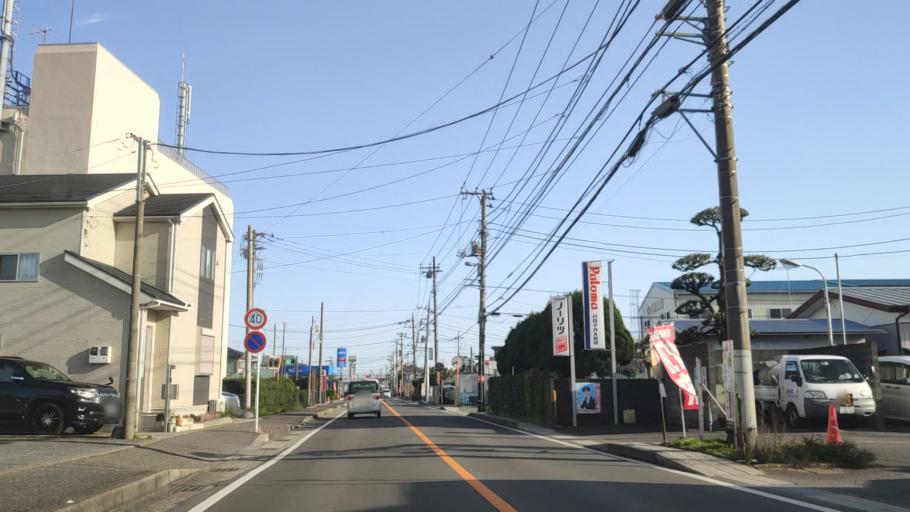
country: JP
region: Kanagawa
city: Zama
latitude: 35.5177
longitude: 139.3328
